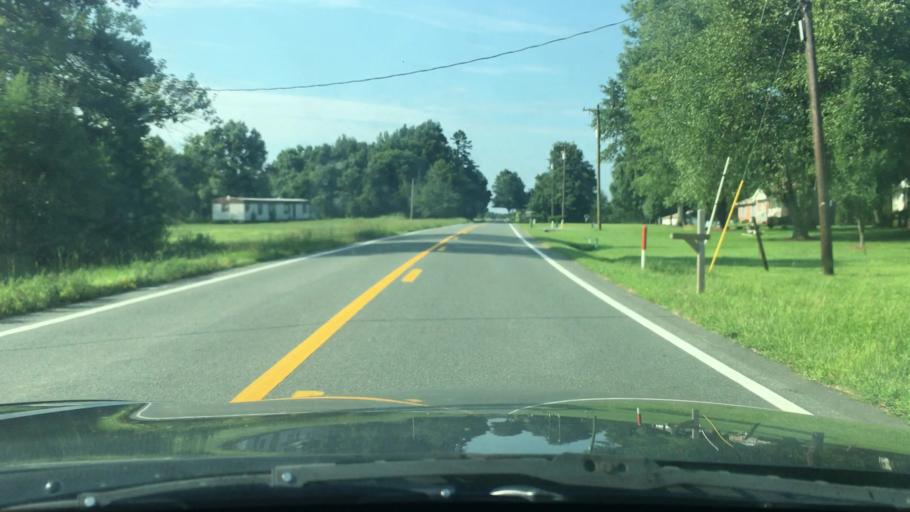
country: US
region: North Carolina
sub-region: Alamance County
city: Green Level
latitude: 36.2307
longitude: -79.3223
